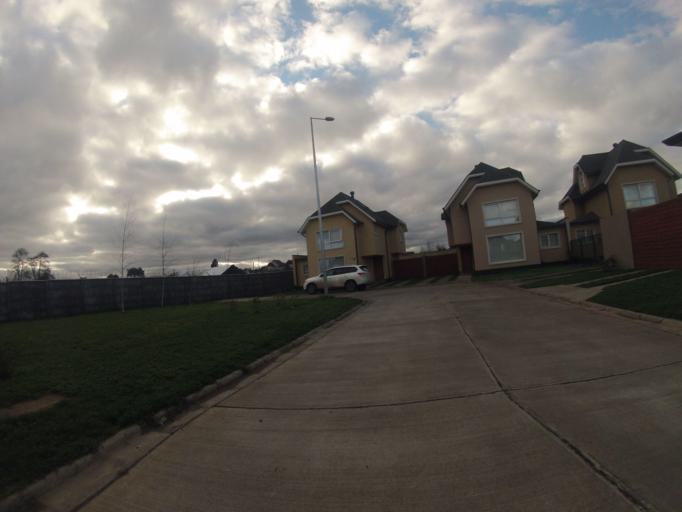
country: CL
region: Araucania
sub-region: Provincia de Cautin
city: Temuco
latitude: -38.7360
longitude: -72.6488
